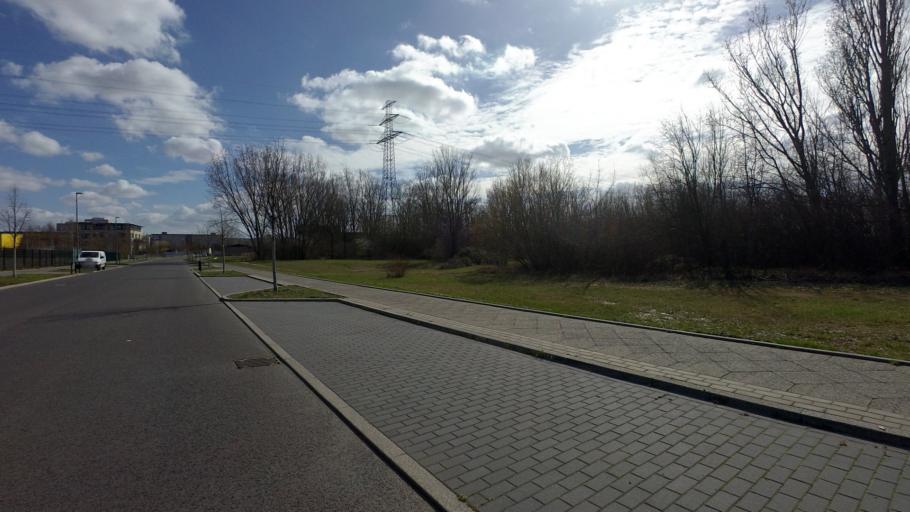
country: DE
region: Berlin
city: Falkenberg
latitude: 52.5599
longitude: 13.5419
